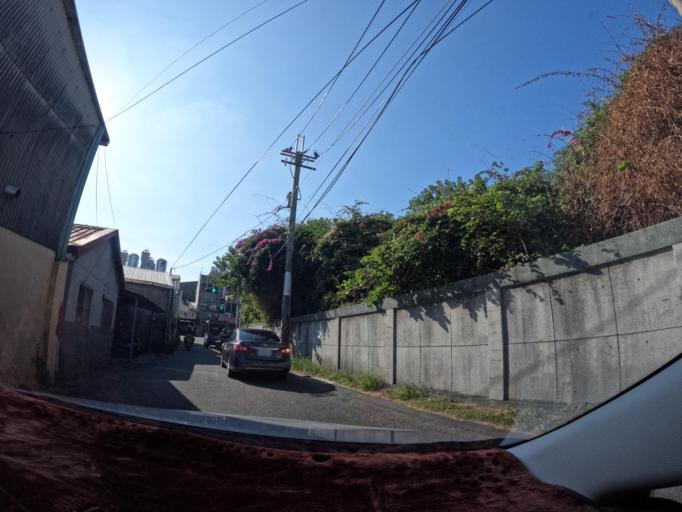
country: TW
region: Taiwan
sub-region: Tainan
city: Tainan
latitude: 23.0203
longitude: 120.2458
